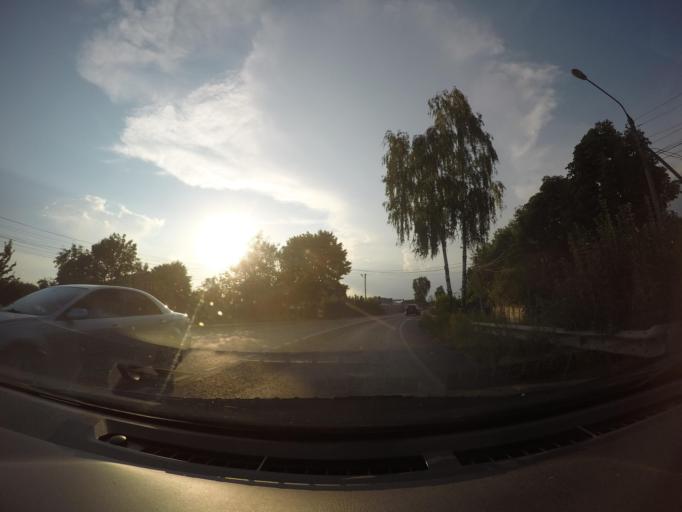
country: RU
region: Moskovskaya
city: Gzhel'
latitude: 55.6072
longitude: 38.3993
